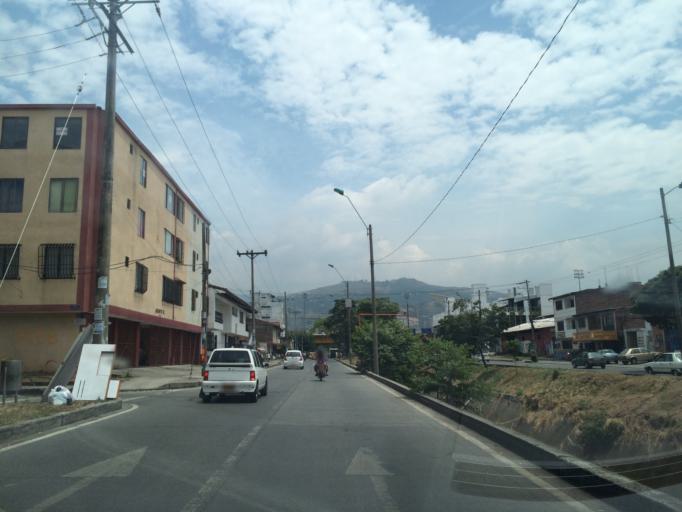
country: CO
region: Valle del Cauca
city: Cali
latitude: 3.4200
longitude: -76.5334
